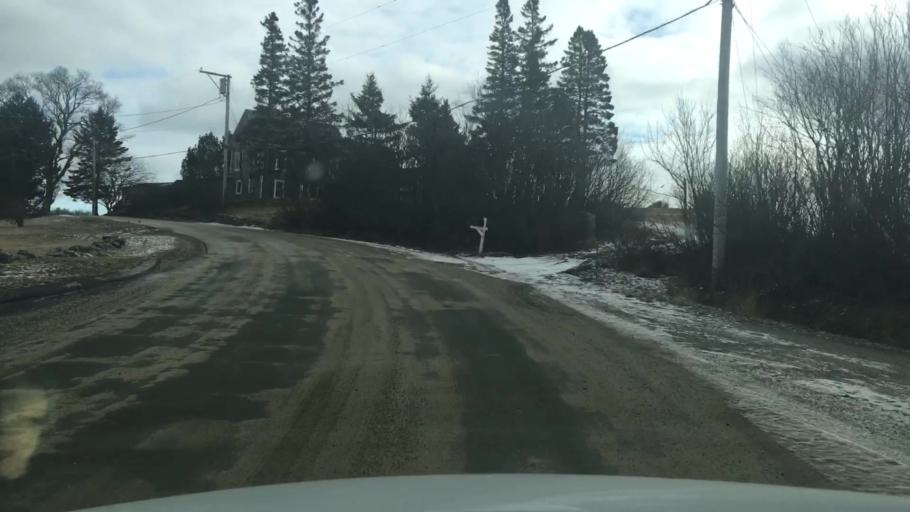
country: US
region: Maine
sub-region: Washington County
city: Machias
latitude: 44.6092
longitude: -67.4764
